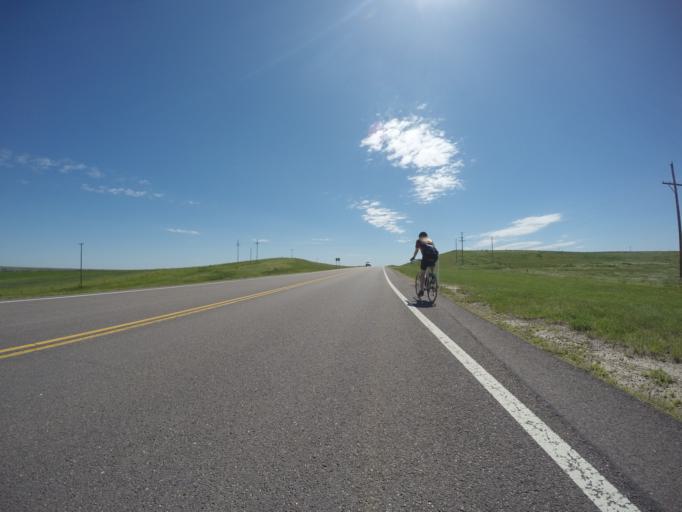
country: US
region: Kansas
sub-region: Rawlins County
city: Atwood
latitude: 39.8134
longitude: -101.0262
